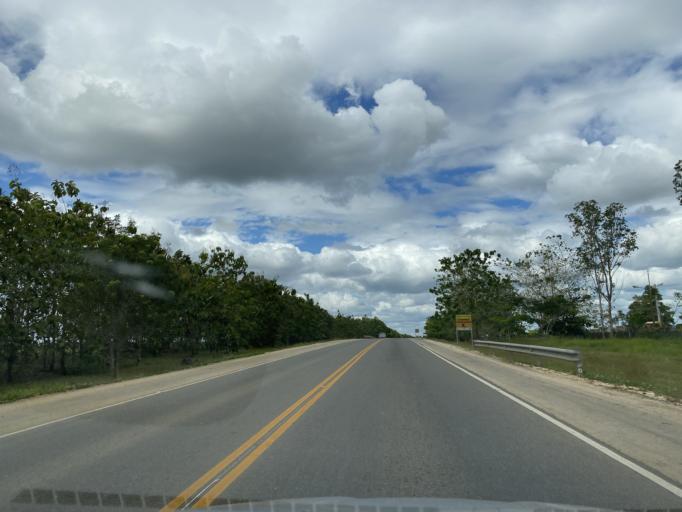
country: DO
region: Santo Domingo
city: Guerra
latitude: 18.5540
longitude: -69.7652
